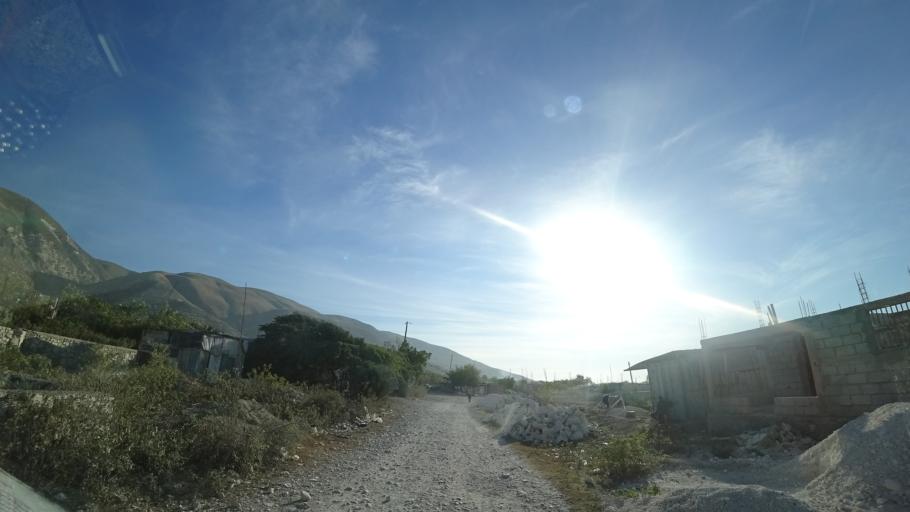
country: HT
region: Ouest
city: Croix des Bouquets
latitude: 18.6696
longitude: -72.2318
